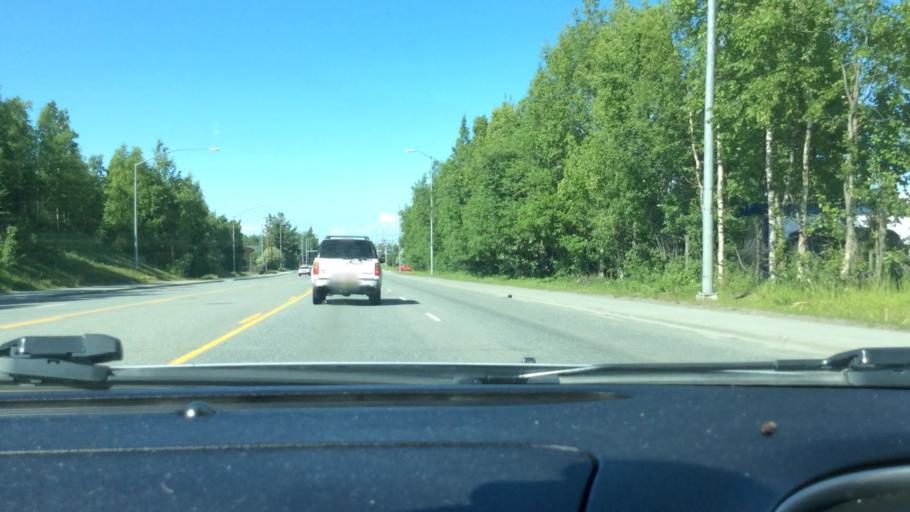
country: US
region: Alaska
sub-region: Anchorage Municipality
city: Anchorage
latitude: 61.2151
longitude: -149.7784
